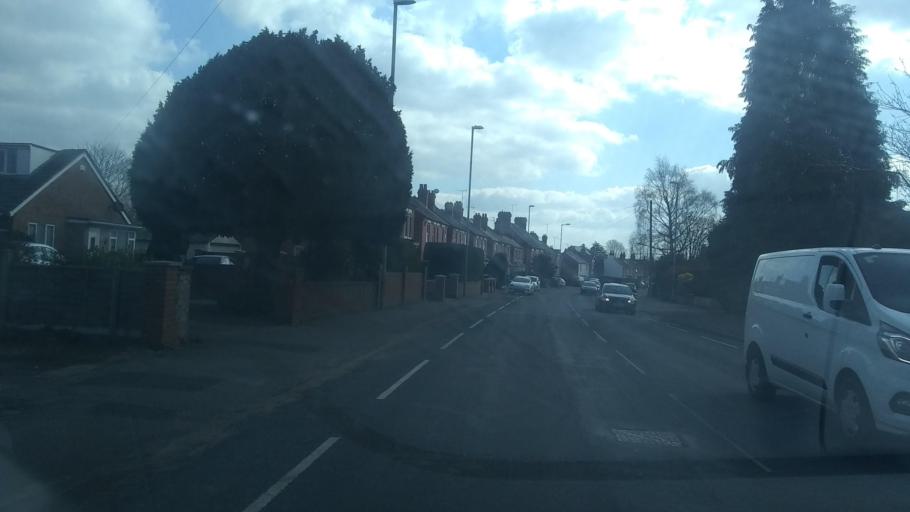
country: GB
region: England
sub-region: Worcestershire
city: Stourport-on-Severn
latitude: 52.3492
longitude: -2.2850
